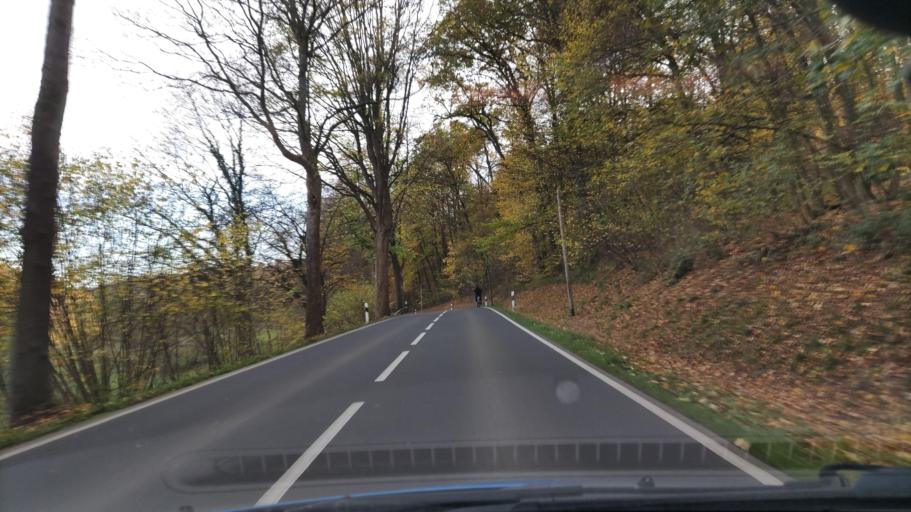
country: DE
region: Lower Saxony
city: Dassel
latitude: 51.7417
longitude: 9.7578
